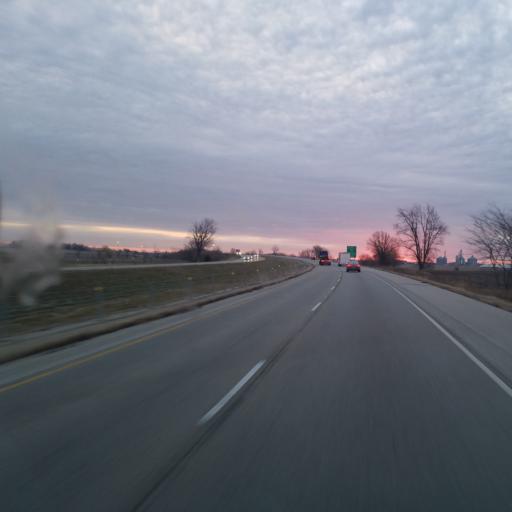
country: US
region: Illinois
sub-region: McLean County
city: Twin Grove
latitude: 40.5414
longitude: -89.0785
